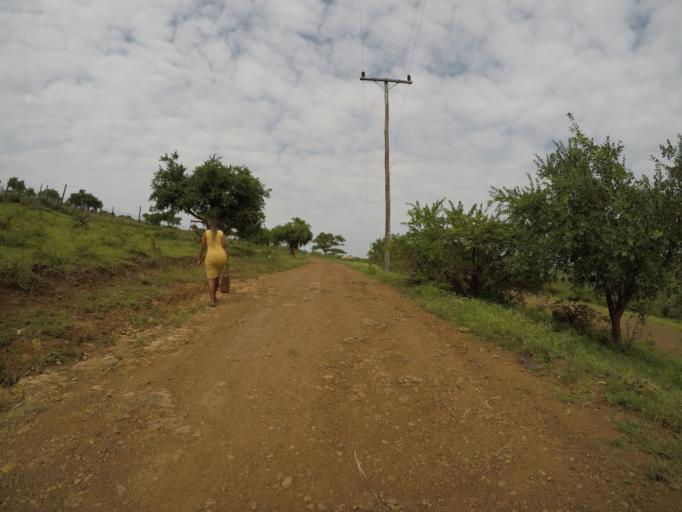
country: ZA
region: KwaZulu-Natal
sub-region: uThungulu District Municipality
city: Empangeni
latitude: -28.6226
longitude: 31.9021
